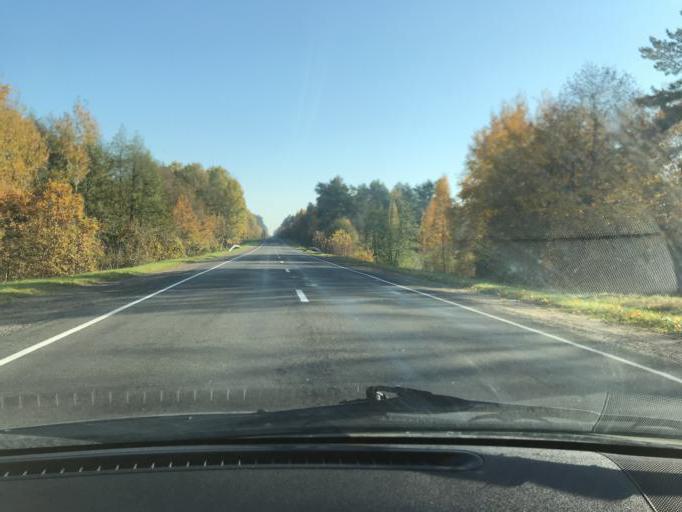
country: BY
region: Brest
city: Lyakhavichy
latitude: 52.9584
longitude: 26.3560
